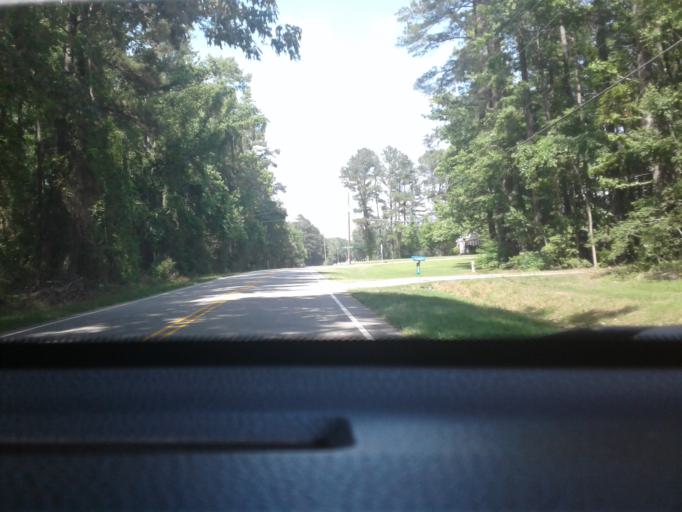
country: US
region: North Carolina
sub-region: Cumberland County
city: Eastover
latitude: 35.1744
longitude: -78.7196
